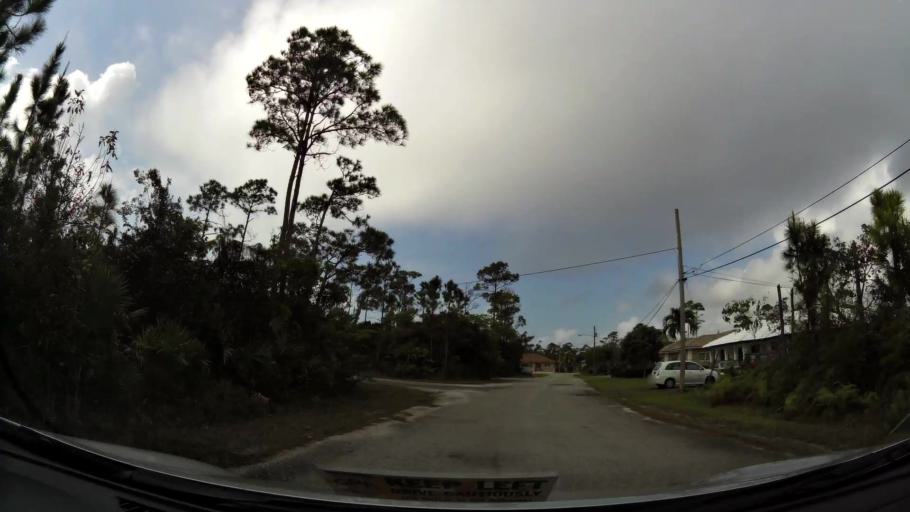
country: BS
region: Freeport
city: Lucaya
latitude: 26.5404
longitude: -78.5949
